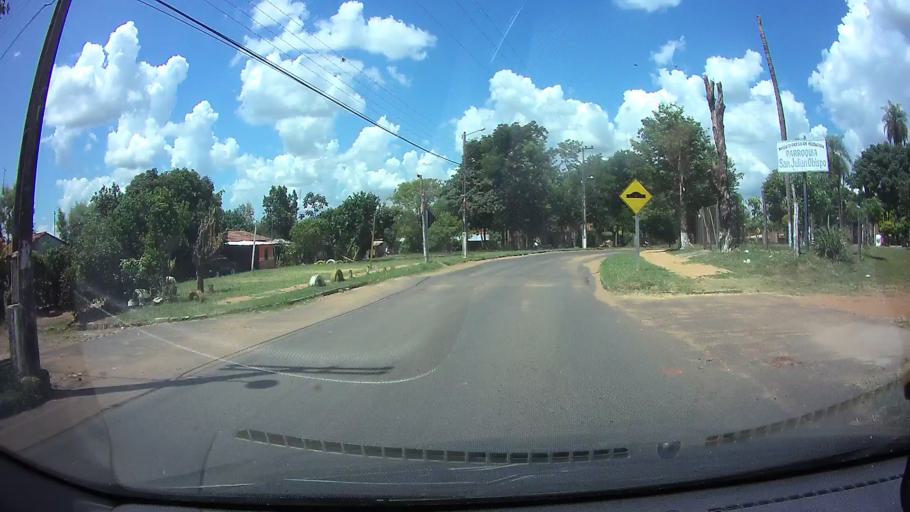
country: PY
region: Central
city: Limpio
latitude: -25.1674
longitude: -57.4406
